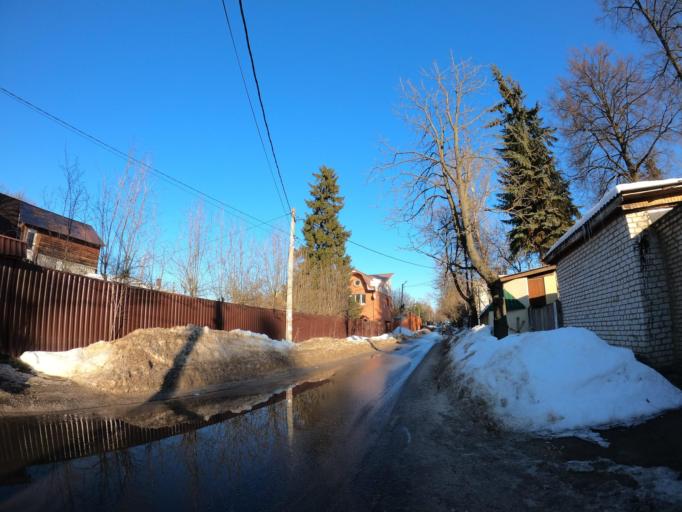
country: RU
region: Moskovskaya
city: Udel'naya
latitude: 55.6389
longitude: 38.0067
